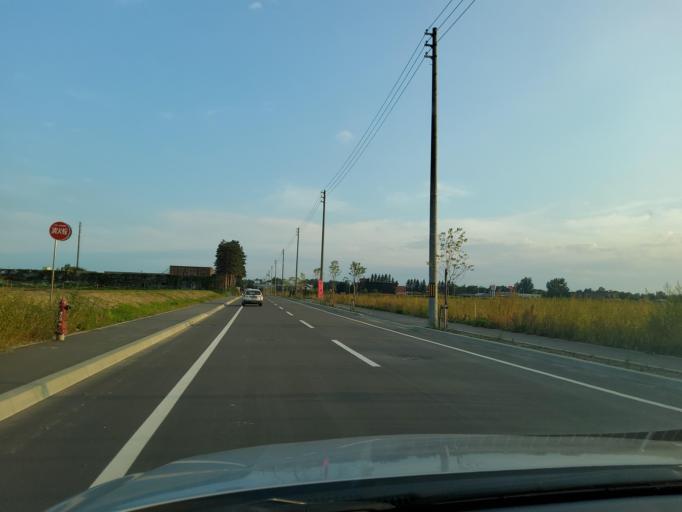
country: JP
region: Hokkaido
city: Obihiro
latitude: 42.9373
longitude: 143.1532
